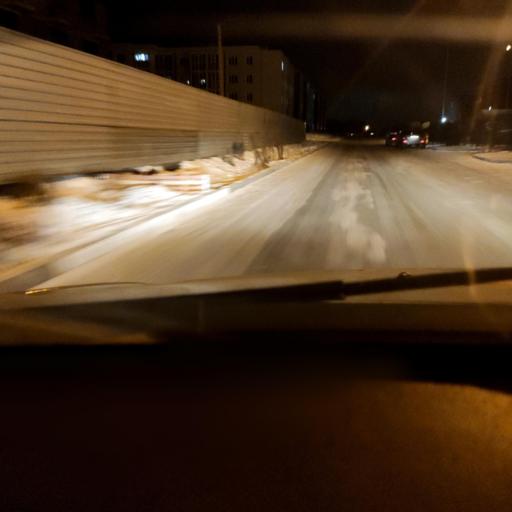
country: RU
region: Bashkortostan
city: Avdon
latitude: 54.7430
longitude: 55.7899
